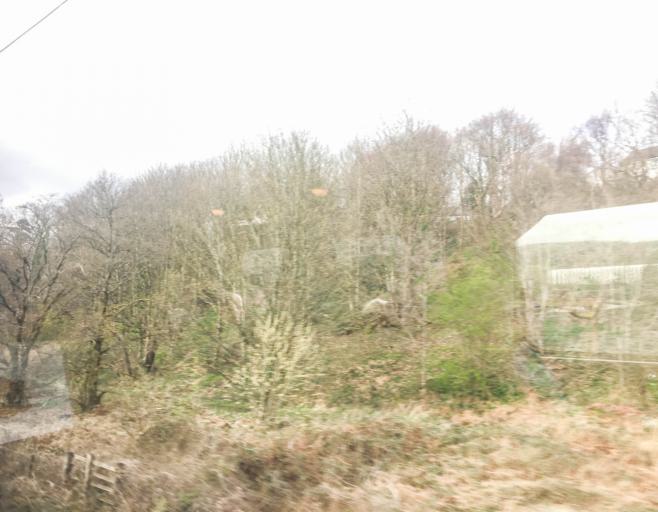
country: GB
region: Scotland
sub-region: West Dunbartonshire
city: Renton
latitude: 55.9473
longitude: -4.6035
